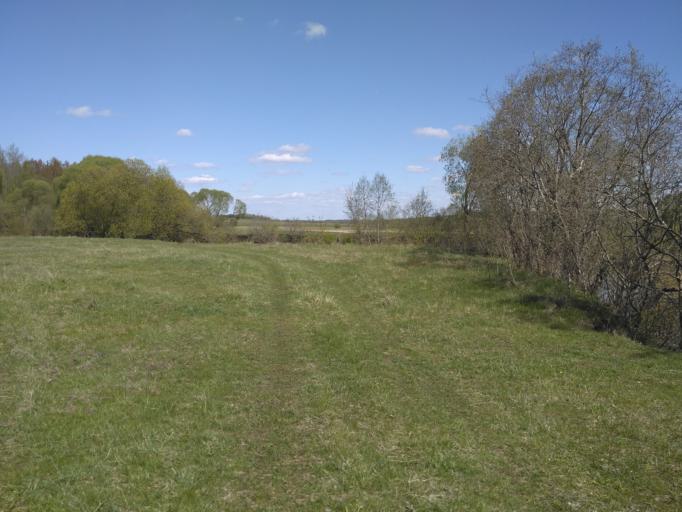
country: BY
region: Mogilev
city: Mstsislaw
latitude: 54.0454
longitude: 31.7031
